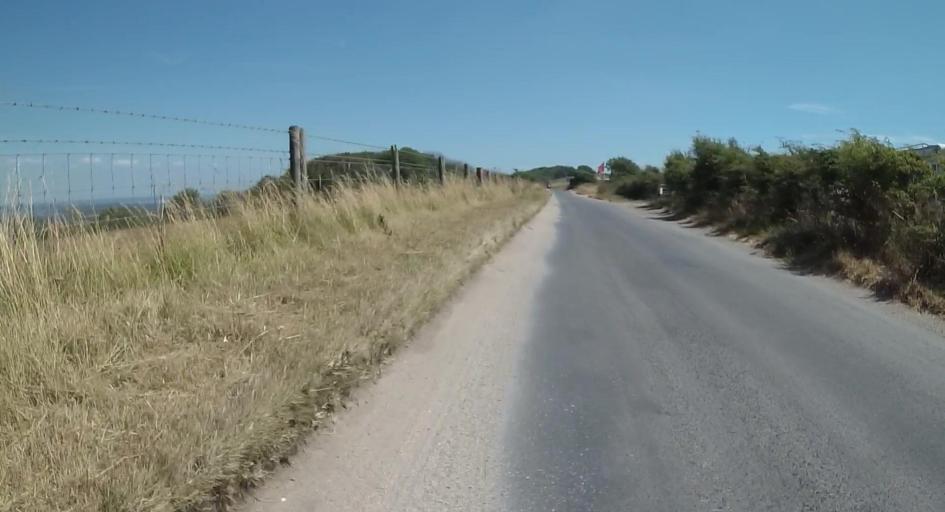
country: GB
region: England
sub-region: Dorset
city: Wareham
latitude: 50.6351
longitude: -2.1375
